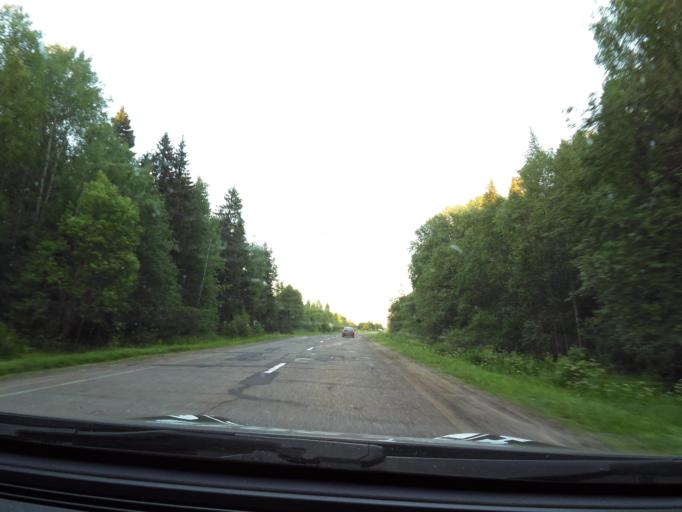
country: RU
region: Jaroslavl
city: Prechistoye
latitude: 58.3939
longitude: 40.4248
